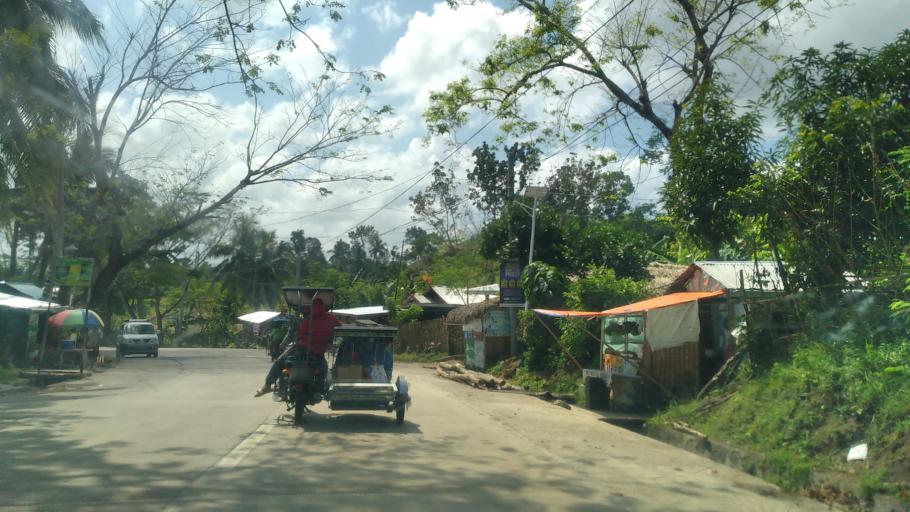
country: PH
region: Calabarzon
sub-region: Province of Quezon
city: Macalelon
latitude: 13.7585
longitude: 122.1419
